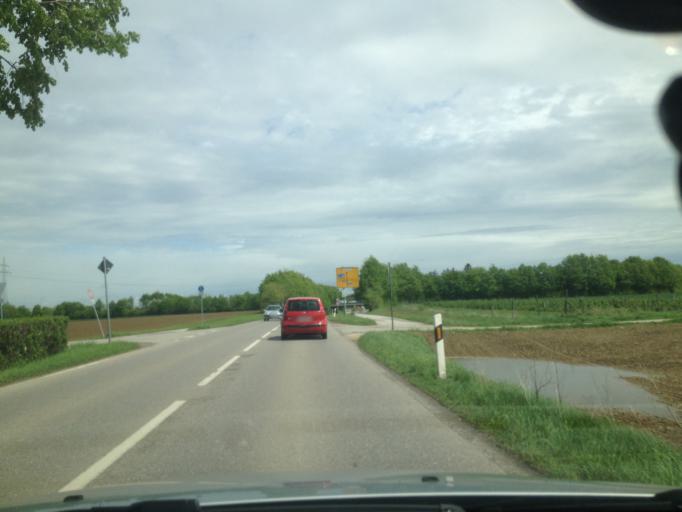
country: DE
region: Bavaria
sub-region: Swabia
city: Konigsbrunn
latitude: 48.3102
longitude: 10.8788
